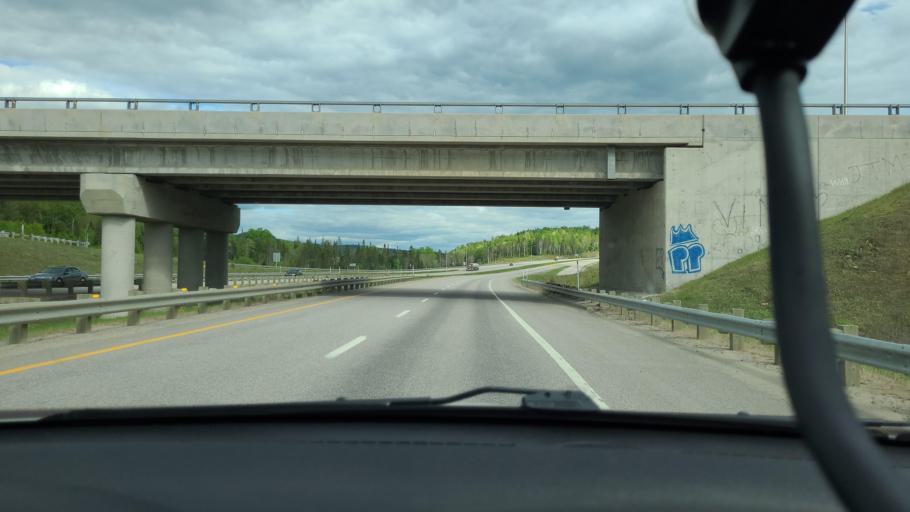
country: CA
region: Quebec
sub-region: Laurentides
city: Labelle
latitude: 46.2763
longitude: -74.7443
